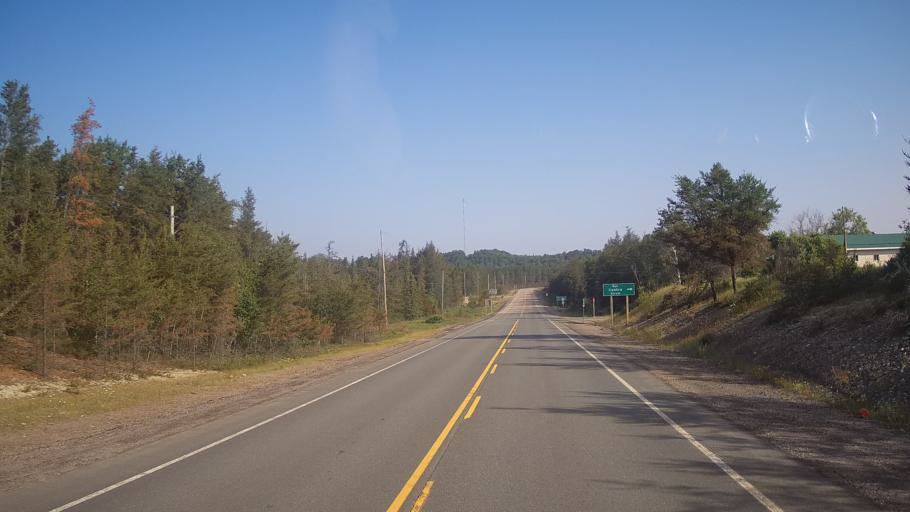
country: CA
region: Ontario
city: Rayside-Balfour
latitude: 46.7032
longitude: -81.5578
